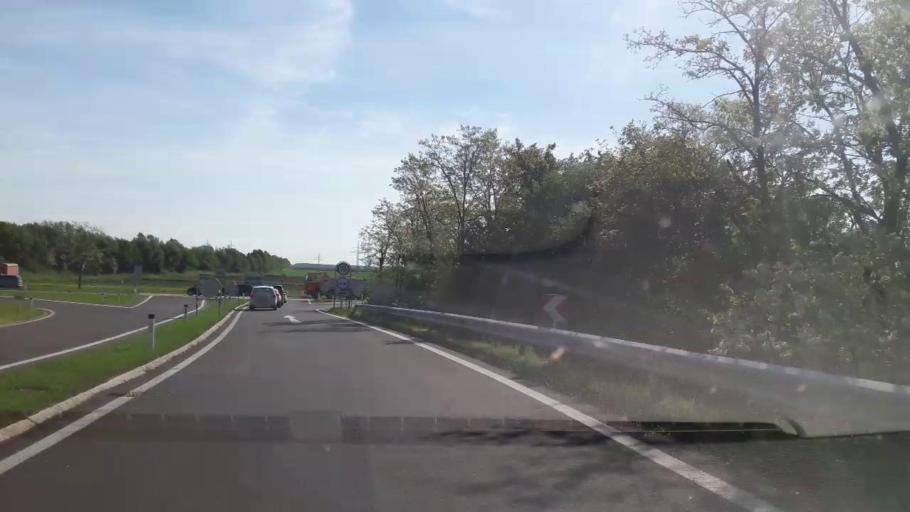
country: AT
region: Burgenland
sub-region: Eisenstadt Stadt
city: Eisenstadt
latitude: 47.8235
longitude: 16.5335
